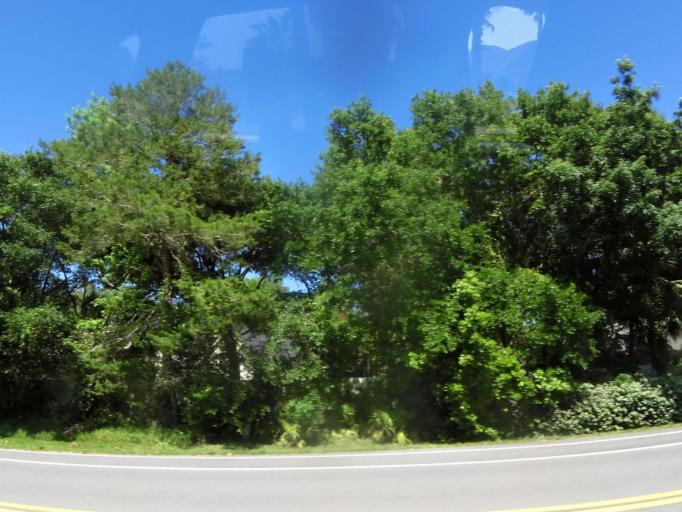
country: US
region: Florida
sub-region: Flagler County
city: Flagler Beach
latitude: 29.4204
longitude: -81.1499
